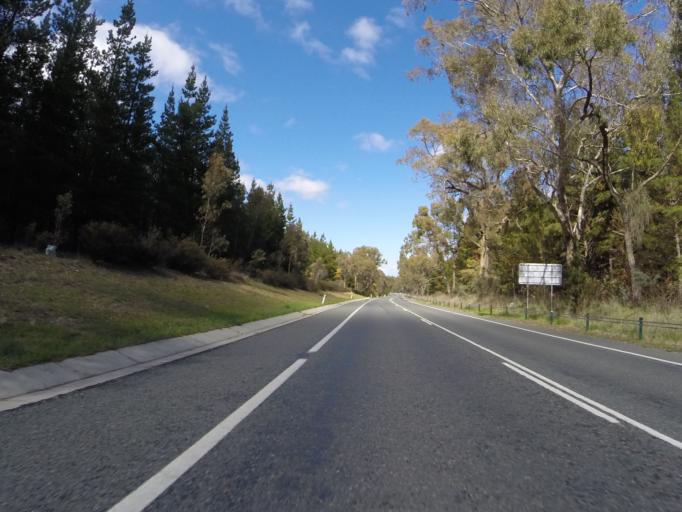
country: AU
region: New South Wales
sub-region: Queanbeyan
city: Queanbeyan
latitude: -35.2710
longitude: 149.2605
